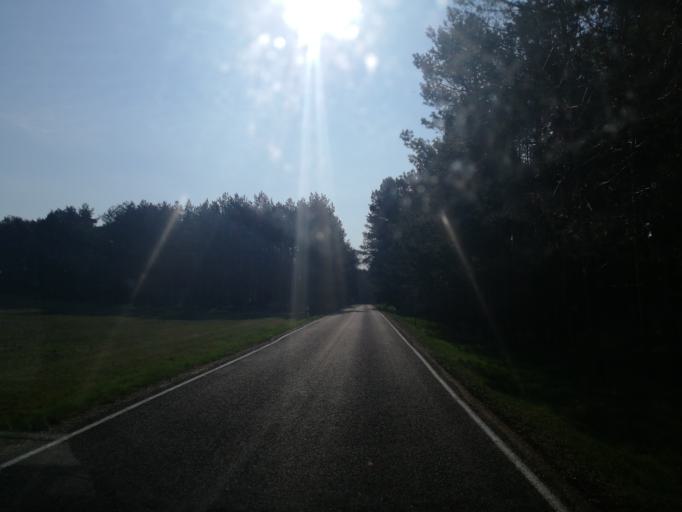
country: DE
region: Brandenburg
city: Sonnewalde
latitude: 51.7743
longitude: 13.6378
